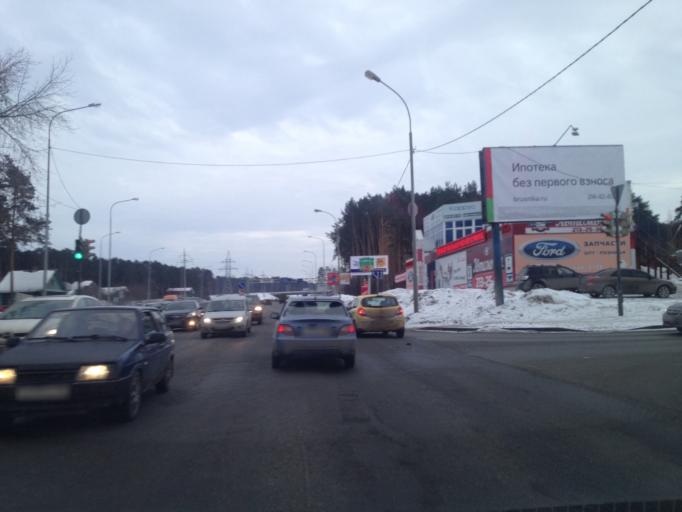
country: RU
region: Sverdlovsk
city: Sovkhoznyy
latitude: 56.7964
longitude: 60.5958
